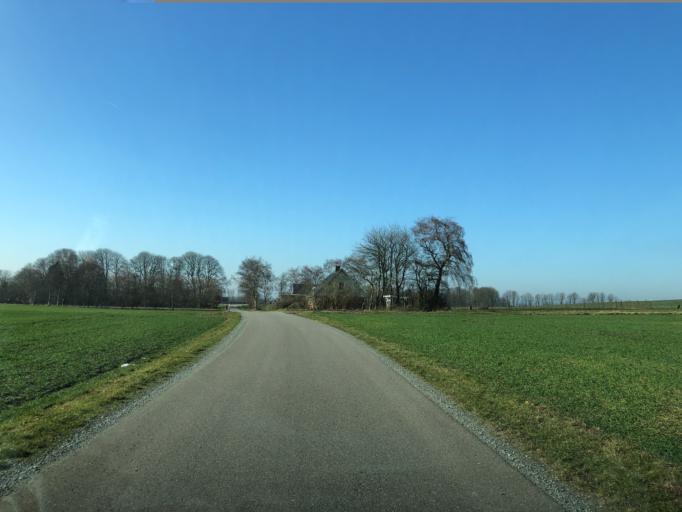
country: DK
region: Central Jutland
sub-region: Skanderborg Kommune
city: Ry
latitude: 56.1963
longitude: 9.7416
